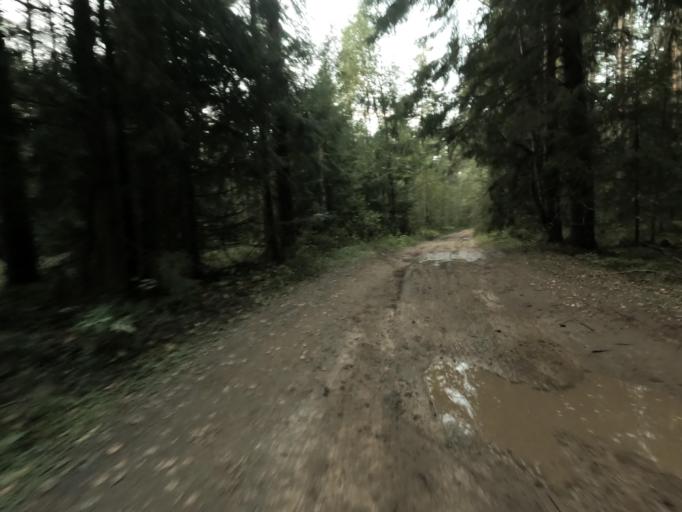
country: RU
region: Leningrad
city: Otradnoye
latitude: 59.8477
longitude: 30.7966
